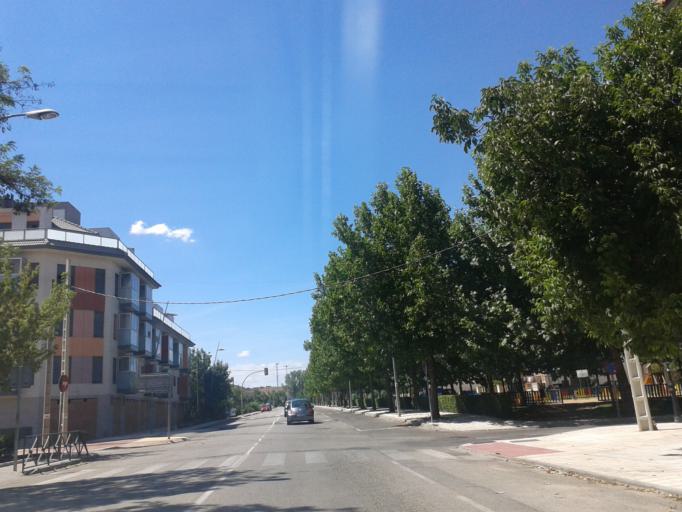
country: ES
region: Castille-La Mancha
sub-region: Provincia de Guadalajara
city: Alovera
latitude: 40.5948
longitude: -3.2524
